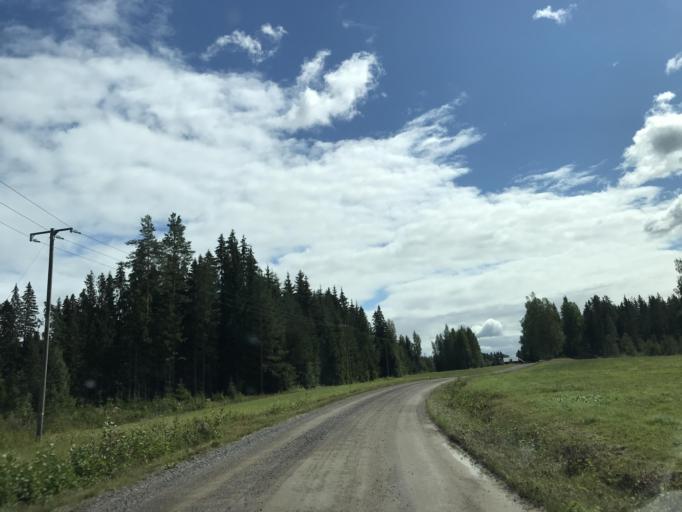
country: FI
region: Uusimaa
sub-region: Helsinki
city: Kaerkoelae
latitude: 60.6337
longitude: 23.8348
